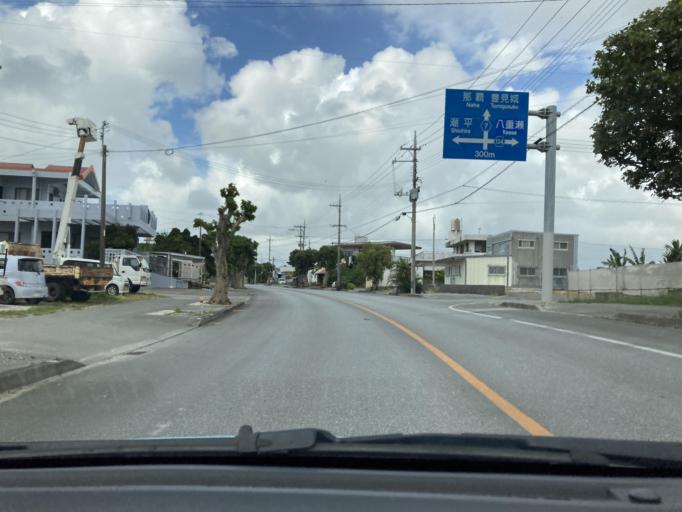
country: JP
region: Okinawa
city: Itoman
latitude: 26.1439
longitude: 127.6936
